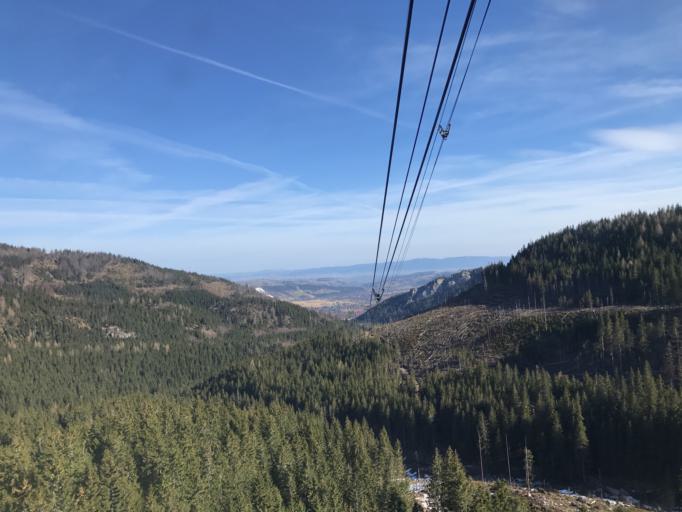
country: PL
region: Lesser Poland Voivodeship
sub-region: Powiat tatrzanski
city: Zakopane
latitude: 49.2551
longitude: 19.9748
